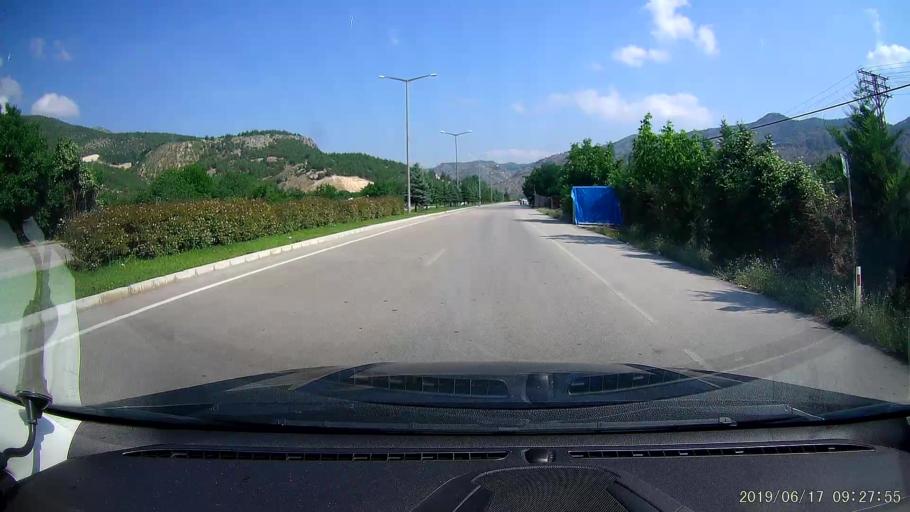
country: TR
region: Amasya
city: Amasya
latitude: 40.6824
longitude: 35.8237
